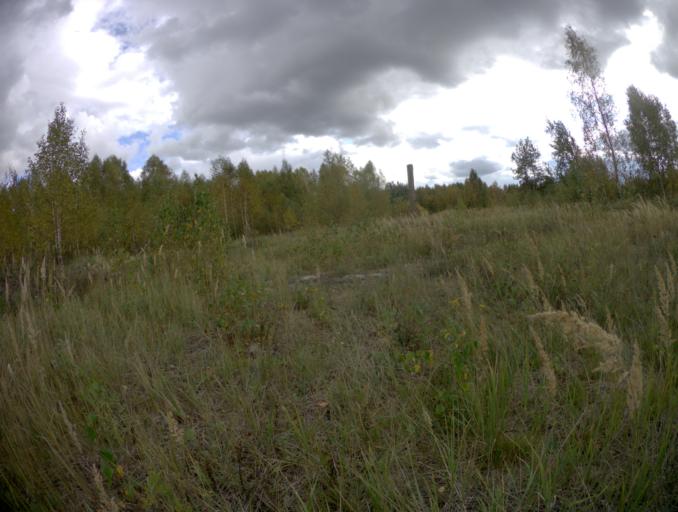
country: RU
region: Vladimir
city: Urshel'skiy
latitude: 55.7766
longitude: 40.1464
